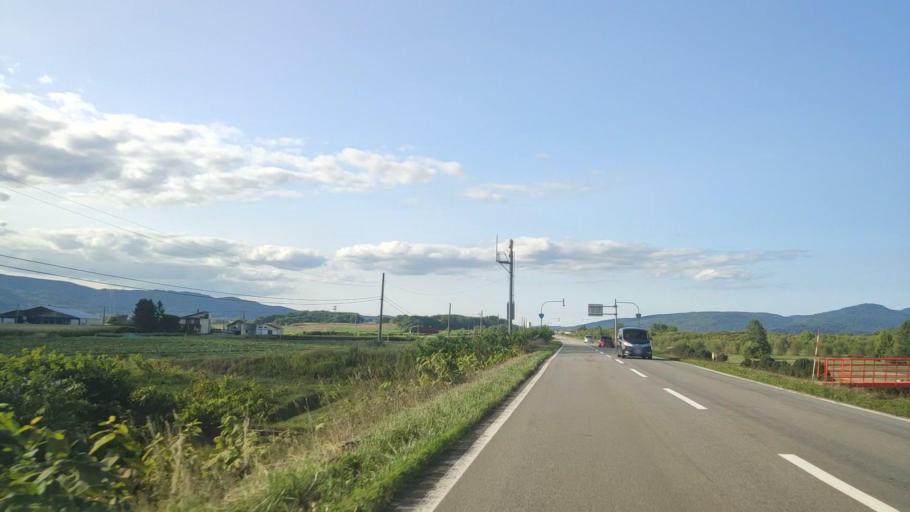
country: JP
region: Hokkaido
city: Nayoro
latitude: 44.8046
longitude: 142.0673
